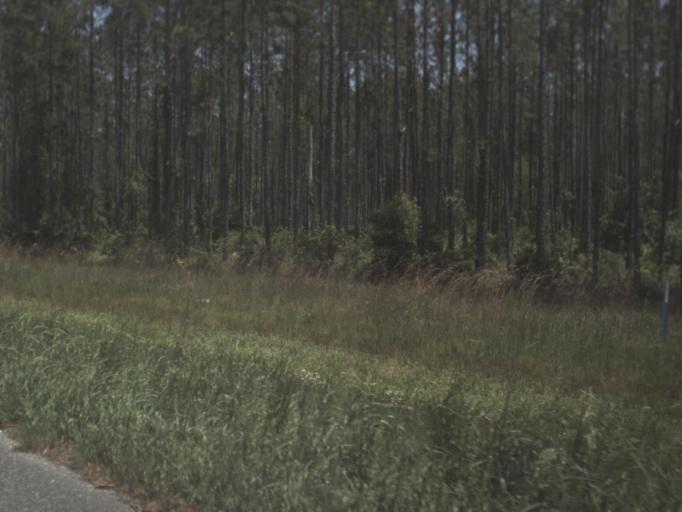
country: US
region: Florida
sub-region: Columbia County
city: Watertown
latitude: 30.1898
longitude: -82.5314
